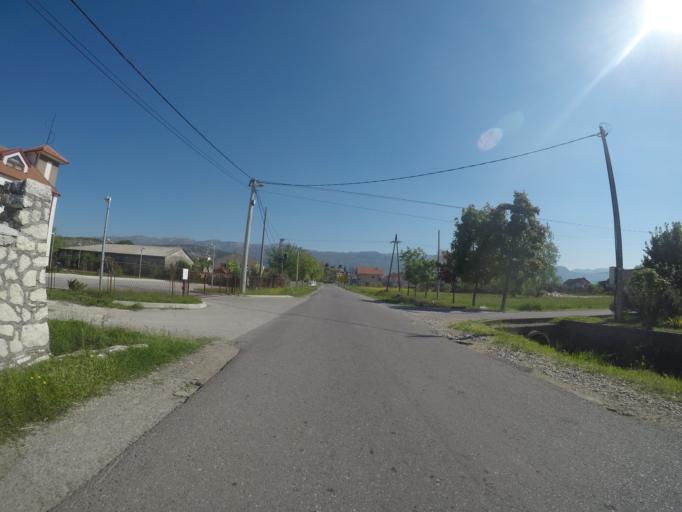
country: ME
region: Danilovgrad
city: Danilovgrad
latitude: 42.5451
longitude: 19.0984
